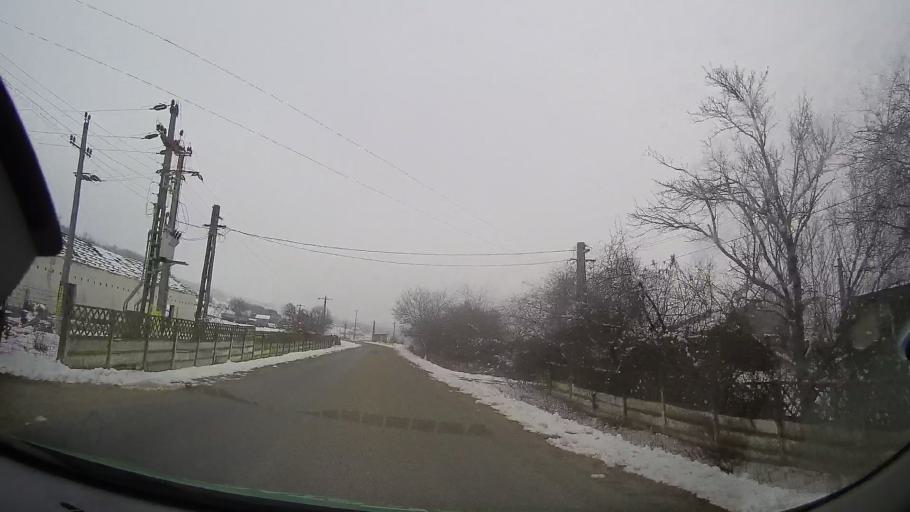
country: RO
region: Bacau
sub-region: Comuna Vultureni
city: Vultureni
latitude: 46.3695
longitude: 27.2824
